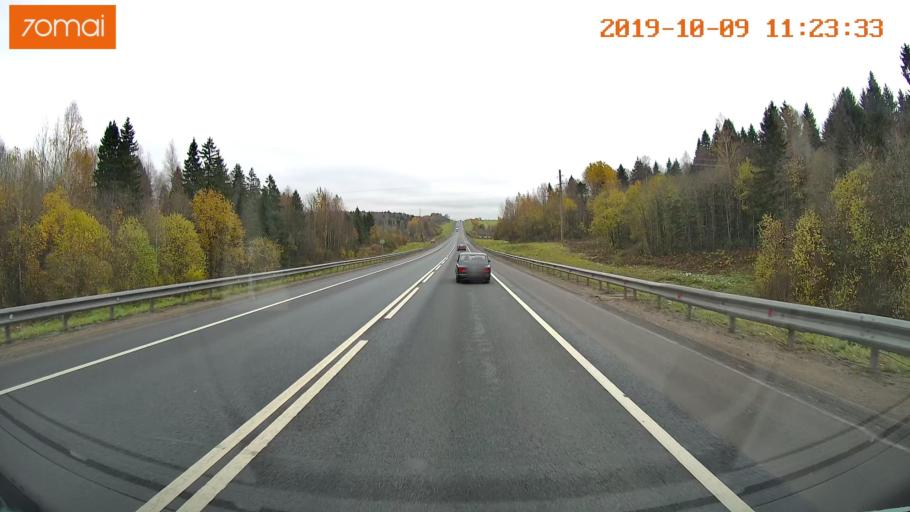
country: RU
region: Vologda
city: Vologda
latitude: 59.1200
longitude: 39.9707
